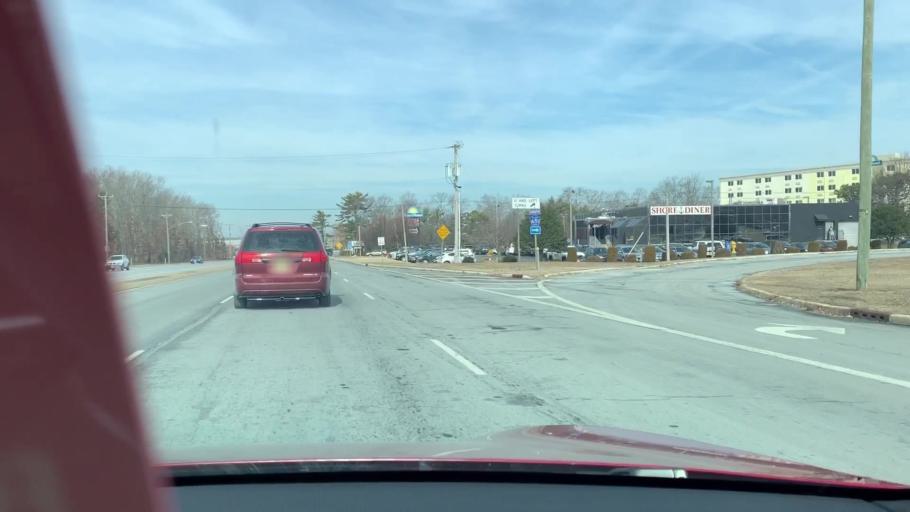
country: US
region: New Jersey
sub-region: Atlantic County
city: Northfield
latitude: 39.3949
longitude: -74.5596
